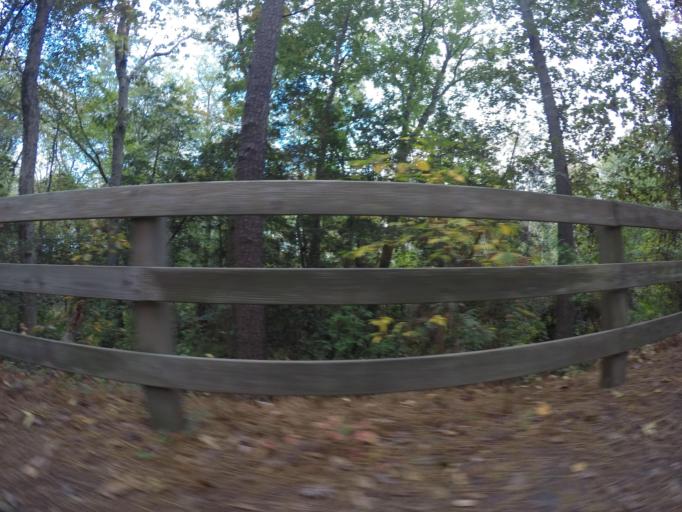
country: US
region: Delaware
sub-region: Sussex County
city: Rehoboth Beach
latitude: 38.7361
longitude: -75.1131
